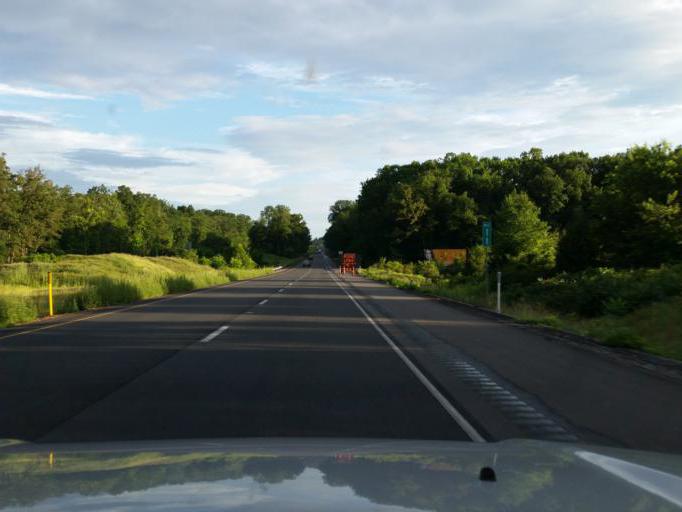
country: US
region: Pennsylvania
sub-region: Adams County
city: Lake Heritage
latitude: 39.8386
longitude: -77.1950
